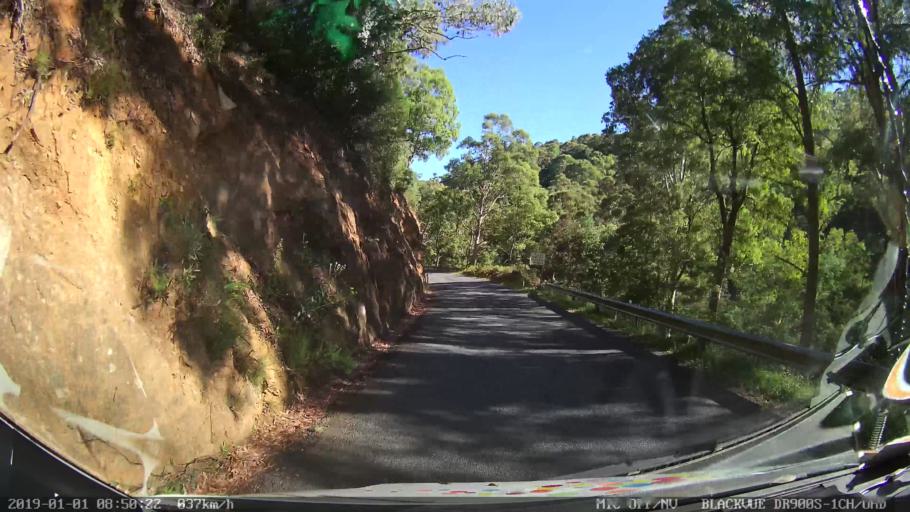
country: AU
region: New South Wales
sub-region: Snowy River
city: Jindabyne
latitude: -36.2768
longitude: 148.2028
